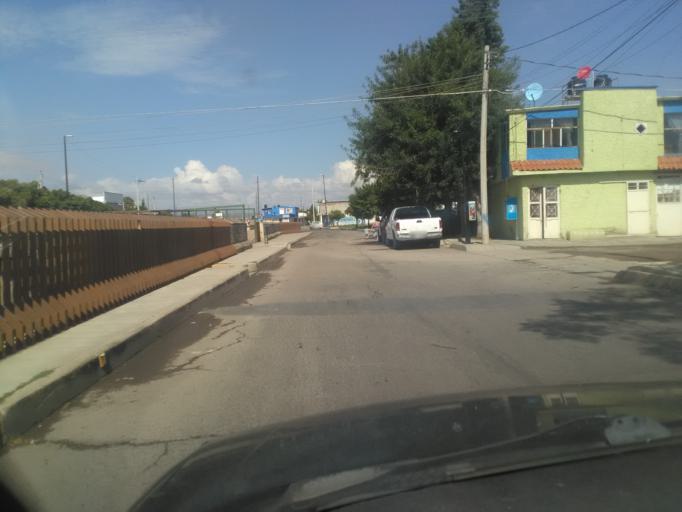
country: MX
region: Durango
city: Victoria de Durango
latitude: 24.0183
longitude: -104.6308
